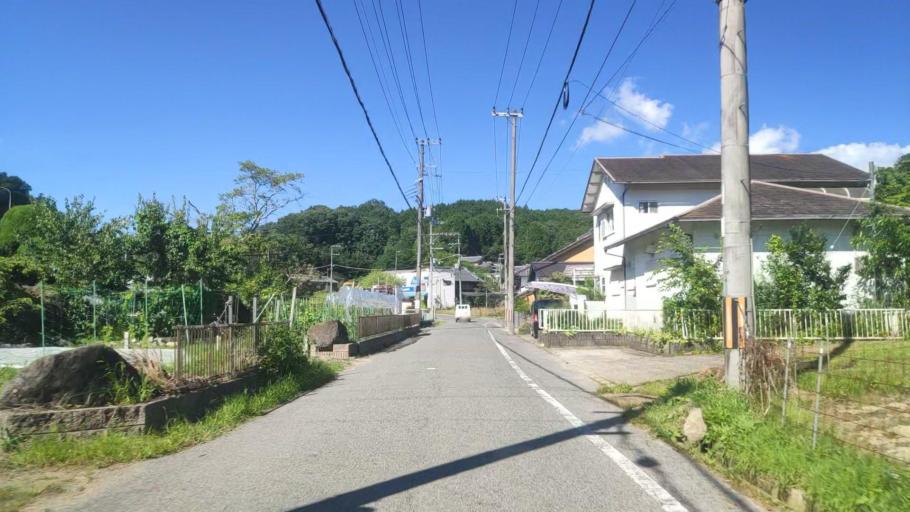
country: JP
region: Nara
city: Haibara-akanedai
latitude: 34.6194
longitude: 135.9805
